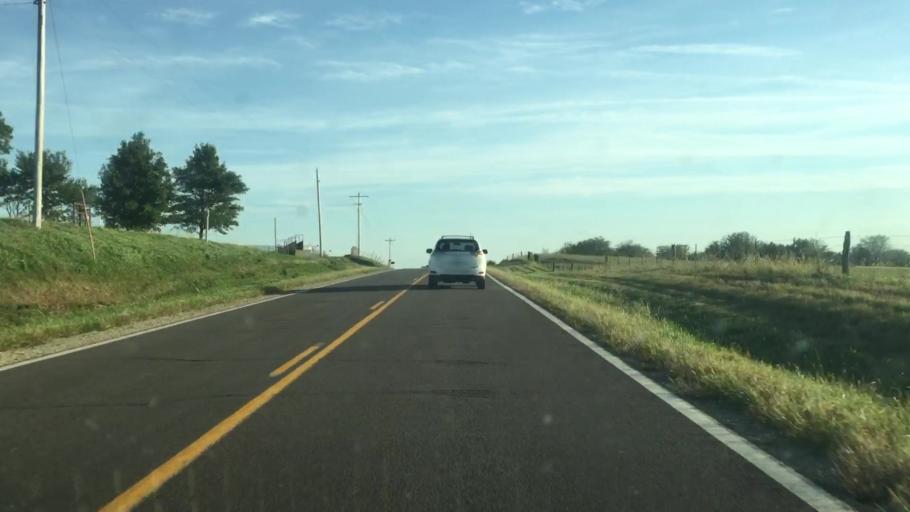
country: US
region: Kansas
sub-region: Brown County
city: Horton
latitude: 39.5756
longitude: -95.5271
